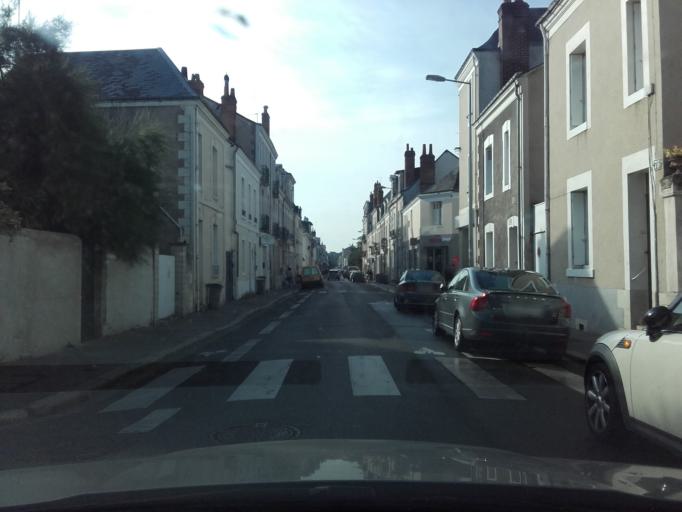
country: FR
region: Centre
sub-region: Departement d'Indre-et-Loire
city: Tours
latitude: 47.3897
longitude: 0.7026
